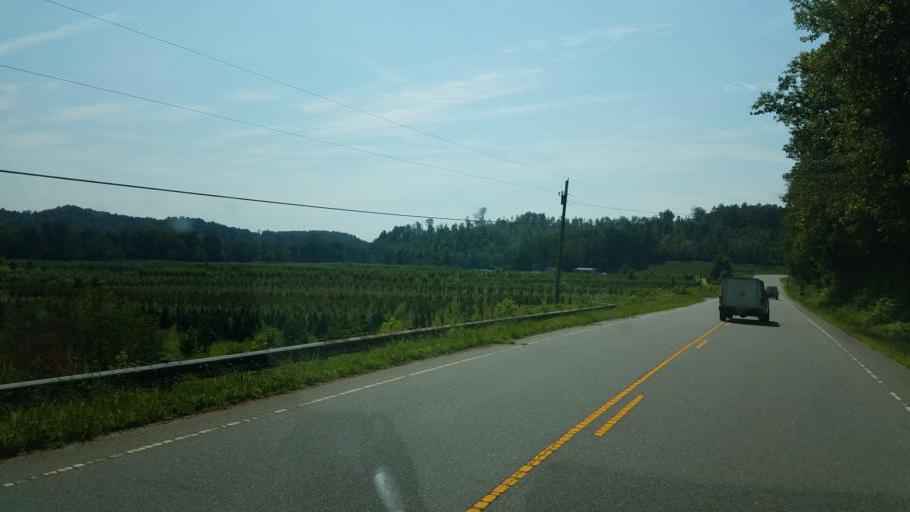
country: US
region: North Carolina
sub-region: Burke County
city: Glen Alpine
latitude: 35.8566
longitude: -81.7834
